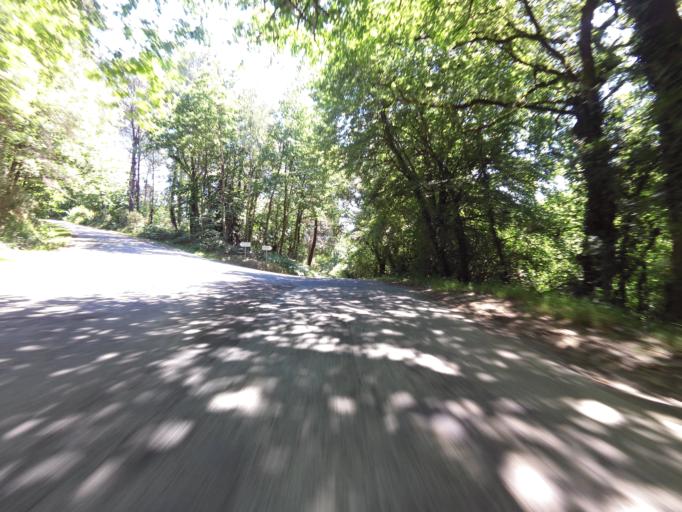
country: FR
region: Brittany
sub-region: Departement du Morbihan
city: Molac
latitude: 47.7216
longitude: -2.4205
